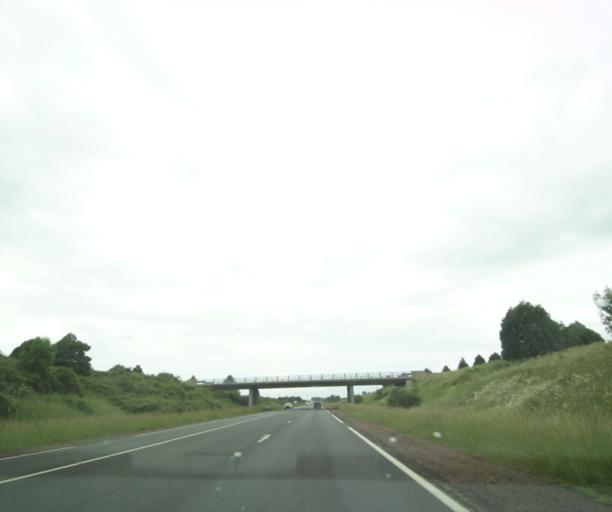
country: FR
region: Poitou-Charentes
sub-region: Departement des Deux-Sevres
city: Airvault
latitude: 46.8266
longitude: -0.2047
